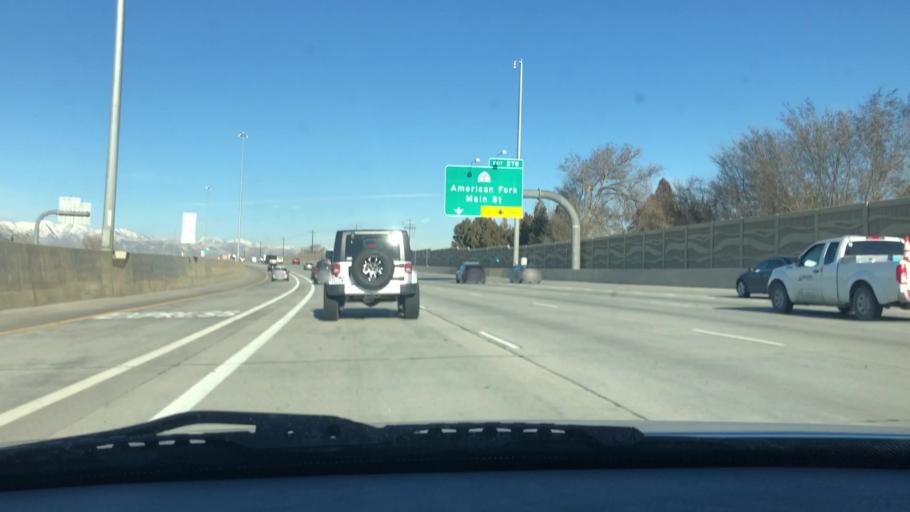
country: US
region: Utah
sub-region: Utah County
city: American Fork
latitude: 40.3713
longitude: -111.8024
